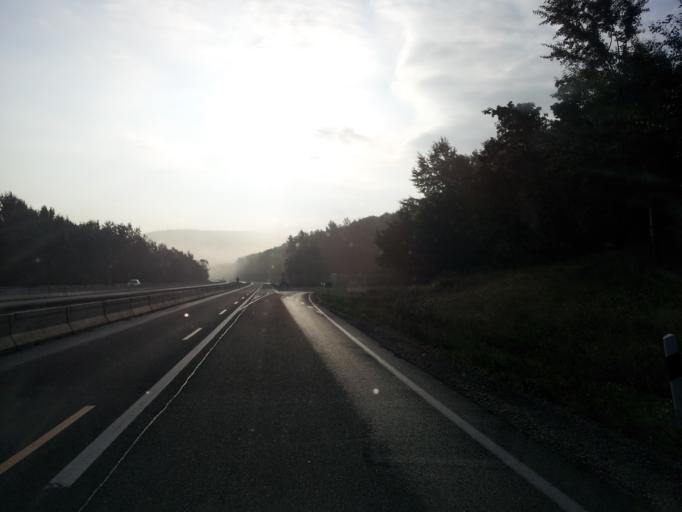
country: HU
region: Pest
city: Godollo
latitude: 47.6127
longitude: 19.3899
